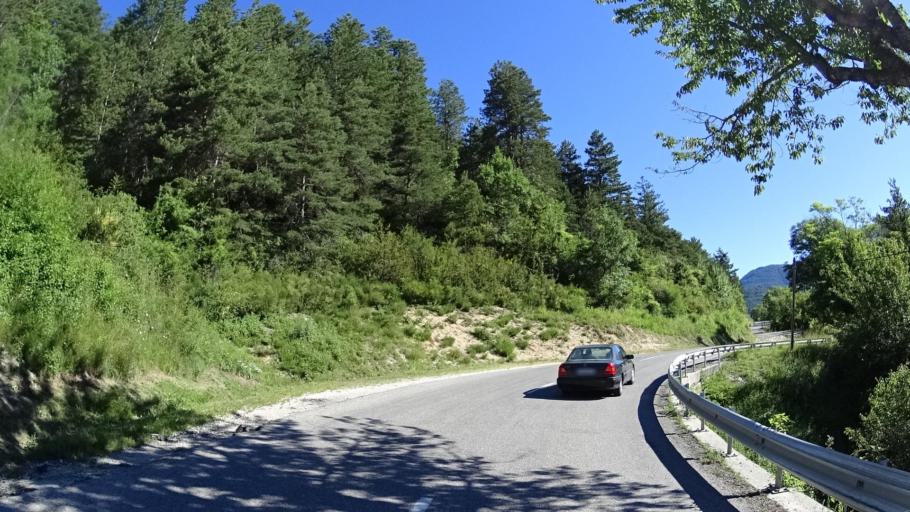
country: FR
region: Provence-Alpes-Cote d'Azur
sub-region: Departement des Alpes-de-Haute-Provence
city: Annot
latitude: 43.9920
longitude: 6.5369
